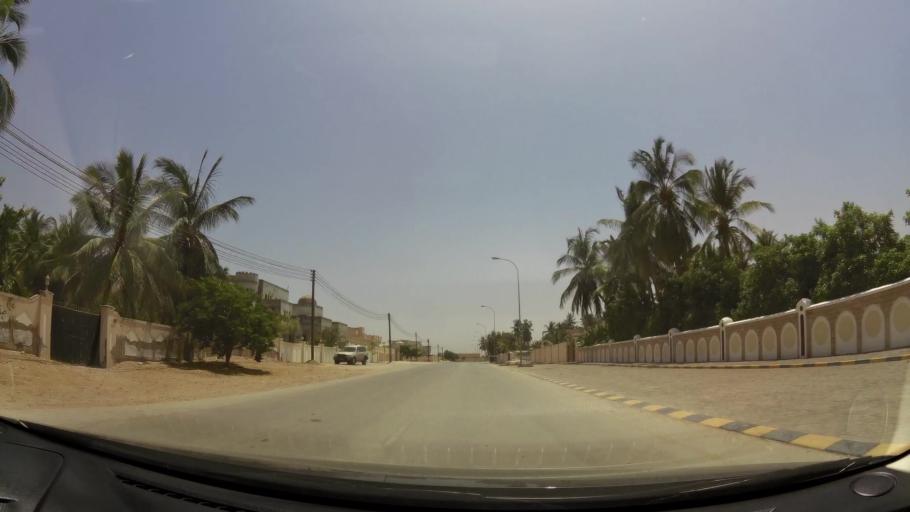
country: OM
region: Zufar
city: Salalah
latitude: 17.0583
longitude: 54.1525
